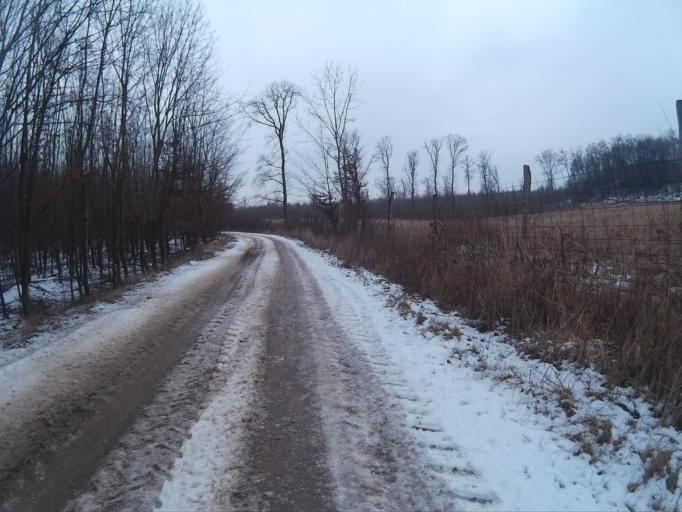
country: HU
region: Komarom-Esztergom
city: Tarjan
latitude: 47.5734
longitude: 18.5234
